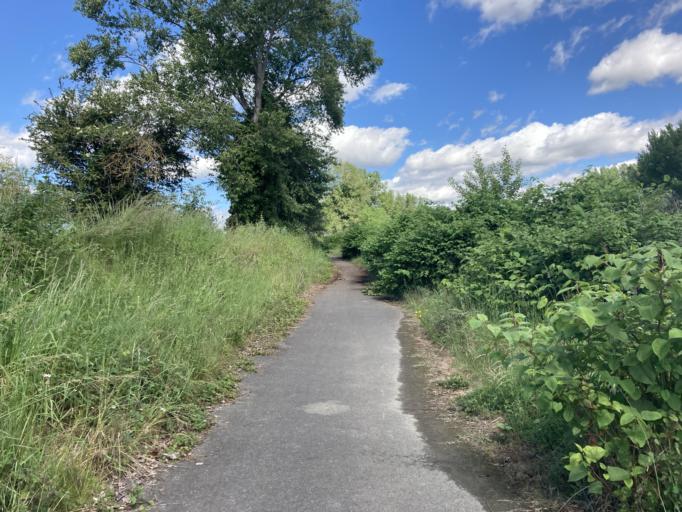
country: FR
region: Aquitaine
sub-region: Departement des Pyrenees-Atlantiques
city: Arbus
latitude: 43.3410
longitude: -0.5024
